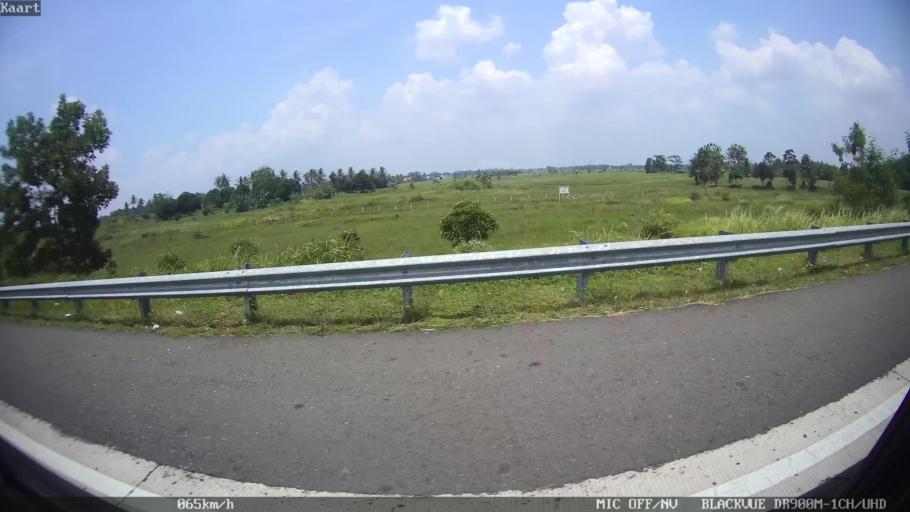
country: ID
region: Lampung
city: Natar
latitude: -5.3006
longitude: 105.2413
